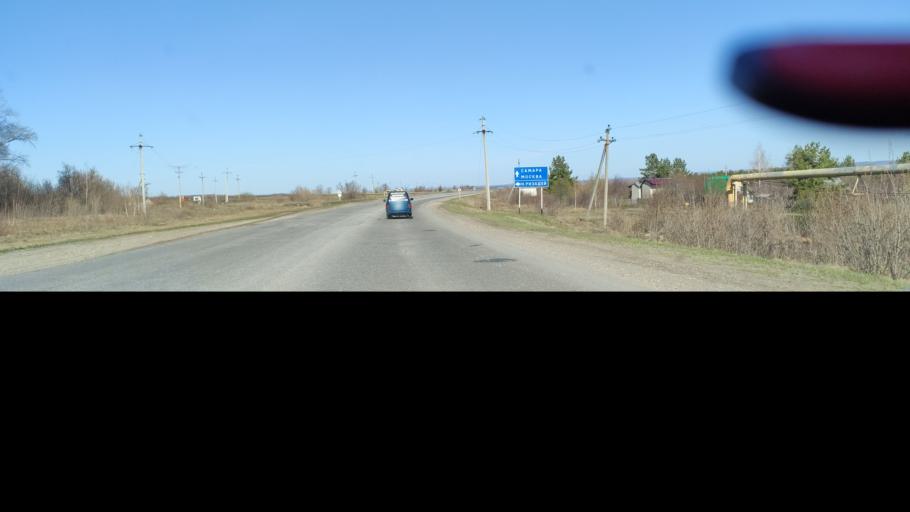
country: RU
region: Samara
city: Varlamovo
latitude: 53.1234
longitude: 48.2987
